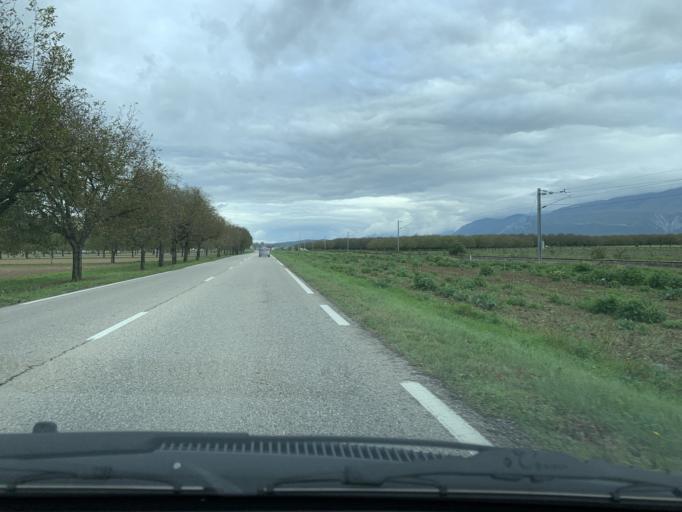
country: FR
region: Rhone-Alpes
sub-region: Departement de l'Isere
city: Chatte
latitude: 45.1314
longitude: 5.2899
